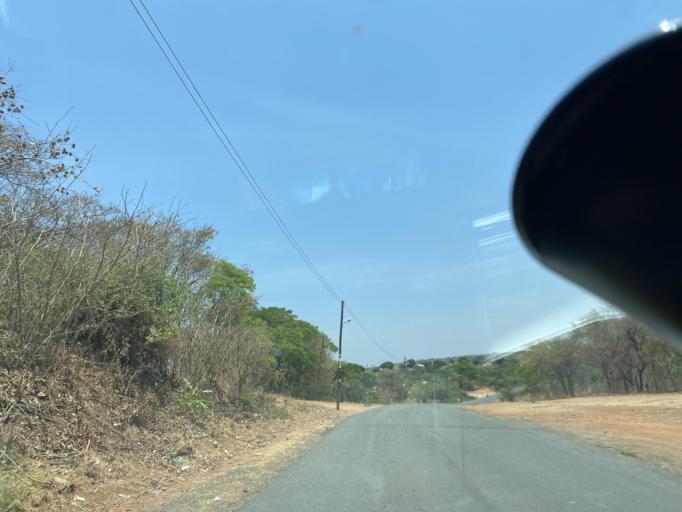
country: ZM
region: Lusaka
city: Kafue
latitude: -15.8675
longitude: 28.4384
